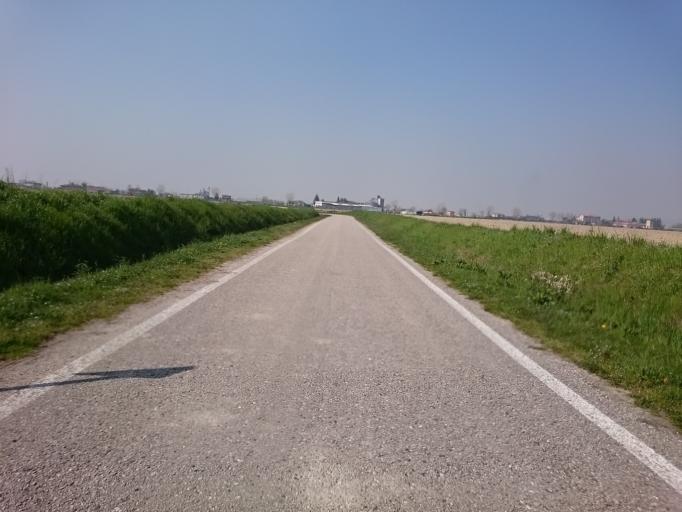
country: IT
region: Veneto
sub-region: Provincia di Padova
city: Sant'Elena
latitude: 45.1896
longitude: 11.6906
